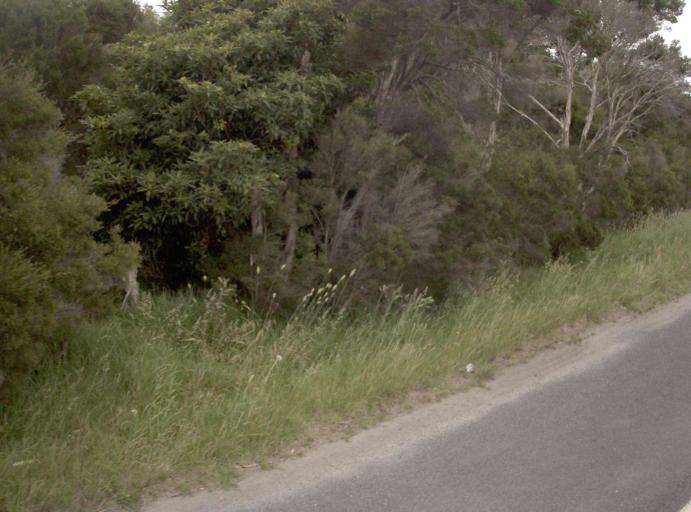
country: AU
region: Victoria
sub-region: Cardinia
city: Koo-Wee-Rup
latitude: -38.2747
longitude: 145.5475
